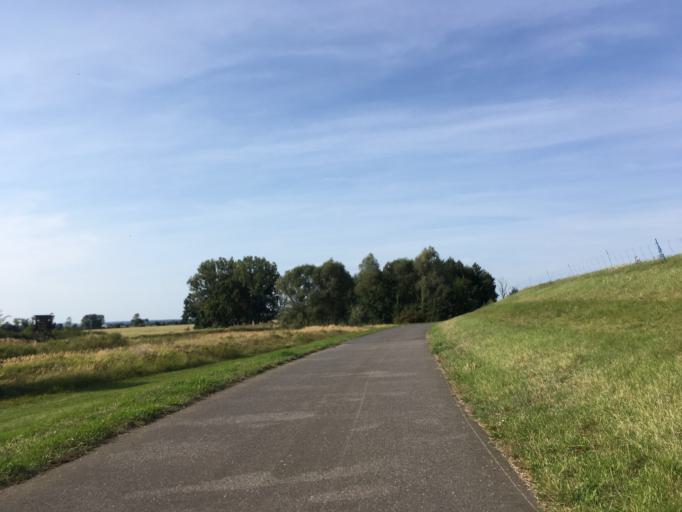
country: DE
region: Brandenburg
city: Vogelsang
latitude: 52.2285
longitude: 14.7062
